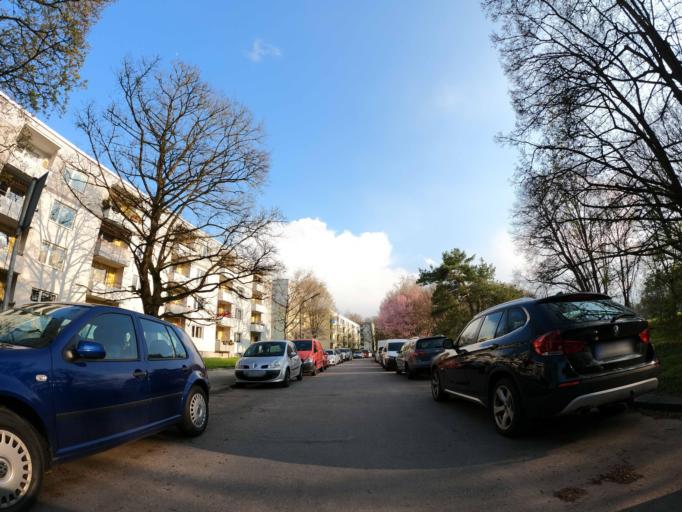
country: DE
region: Bavaria
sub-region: Upper Bavaria
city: Bogenhausen
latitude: 48.1095
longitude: 11.6114
